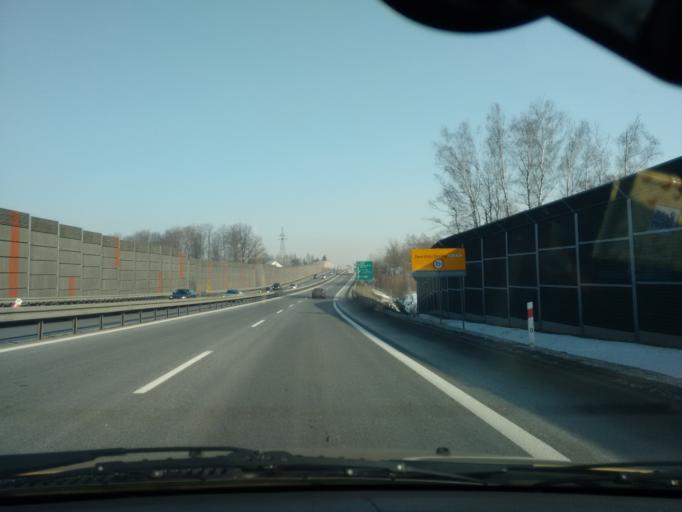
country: PL
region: Silesian Voivodeship
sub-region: Powiat bielski
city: Mazancowice
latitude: 49.8473
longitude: 19.0149
